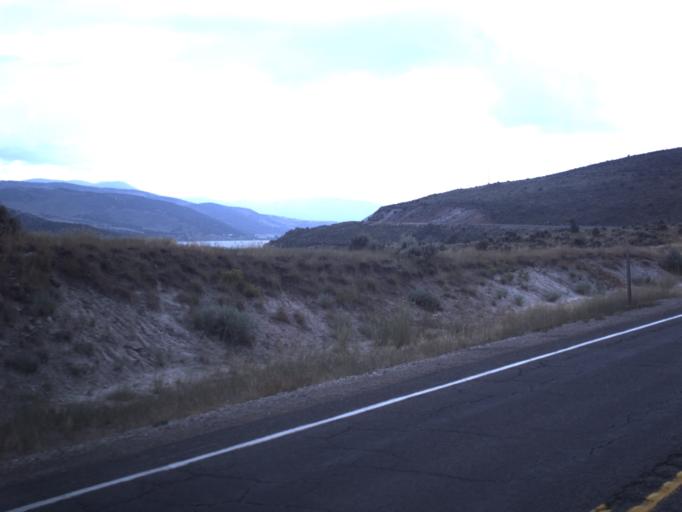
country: US
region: Utah
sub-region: Summit County
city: Oakley
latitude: 40.7743
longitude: -111.4081
